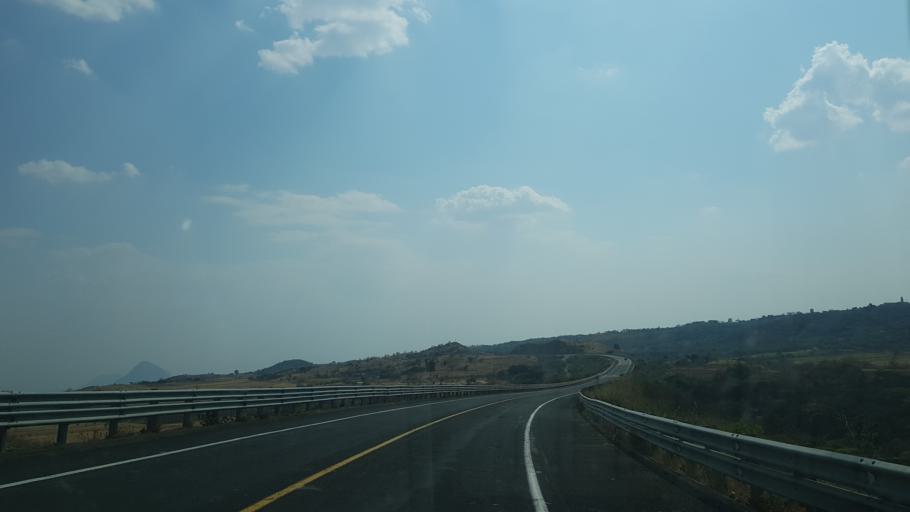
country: MX
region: Puebla
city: San Juan Amecac
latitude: 18.8131
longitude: -98.6972
